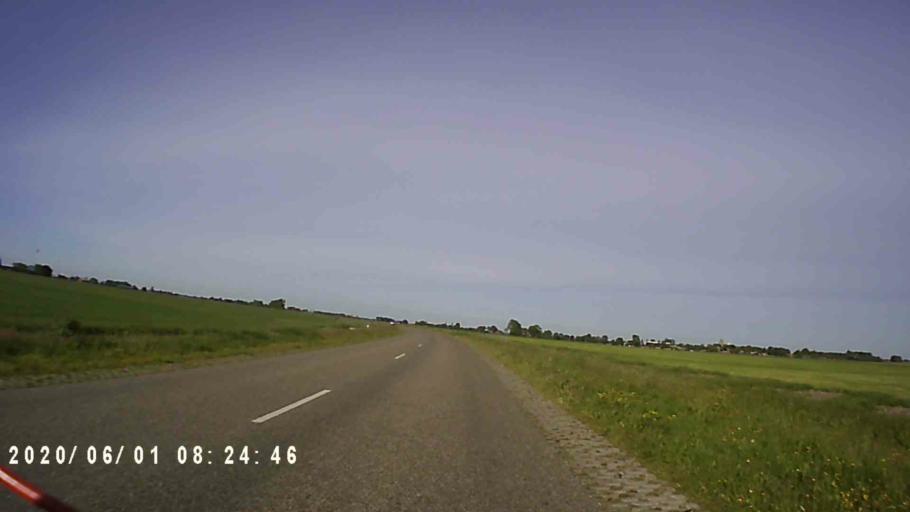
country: NL
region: Friesland
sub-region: Gemeente Ferwerderadiel
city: Burdaard
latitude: 53.3029
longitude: 5.8688
